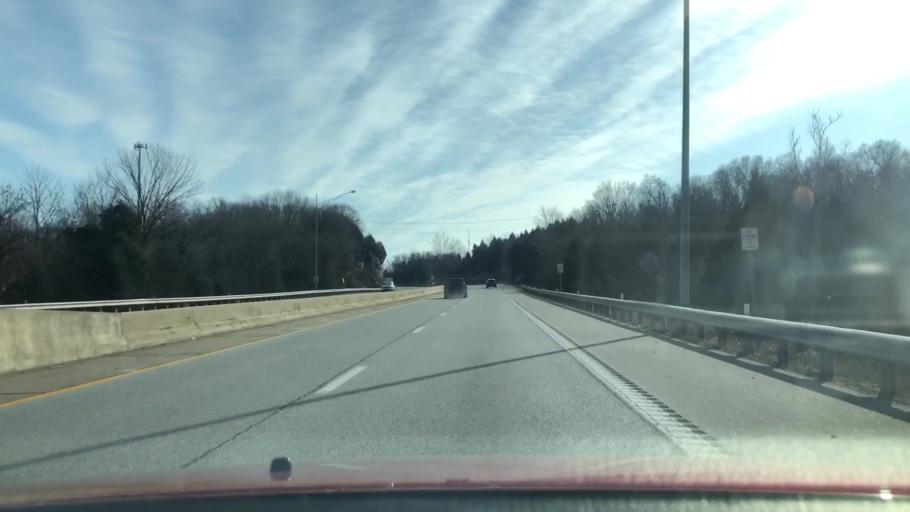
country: US
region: Missouri
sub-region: Christian County
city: Ozark
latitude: 37.1232
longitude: -93.2244
